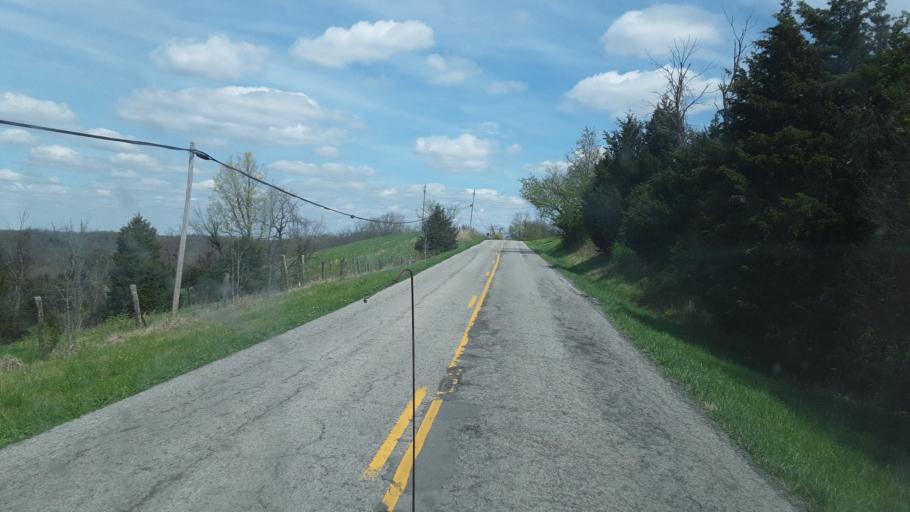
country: US
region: Kentucky
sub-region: Owen County
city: Owenton
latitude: 38.6424
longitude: -84.7547
